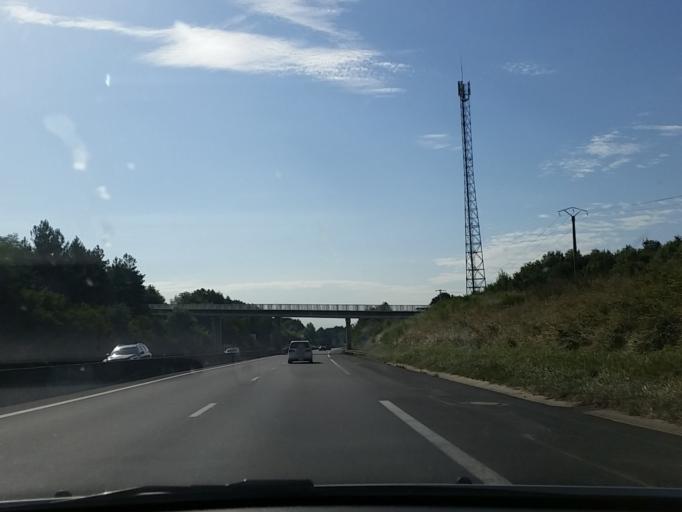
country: FR
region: Centre
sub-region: Departement du Cher
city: Vierzon
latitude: 47.2302
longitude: 2.1008
